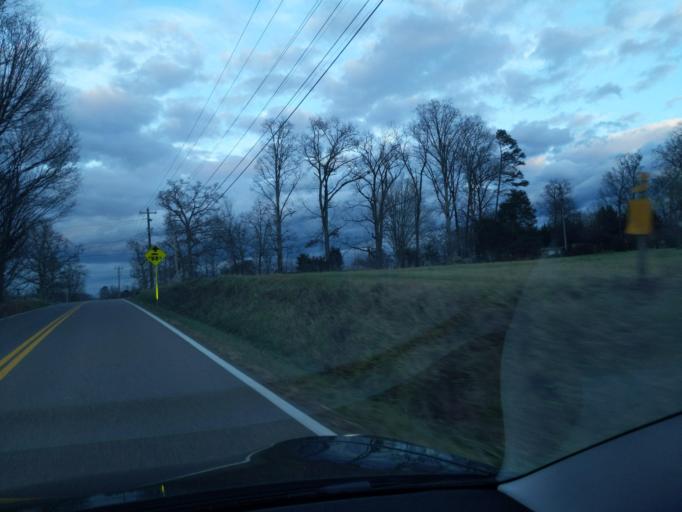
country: US
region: Tennessee
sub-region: Jefferson County
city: White Pine
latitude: 36.0890
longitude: -83.3637
